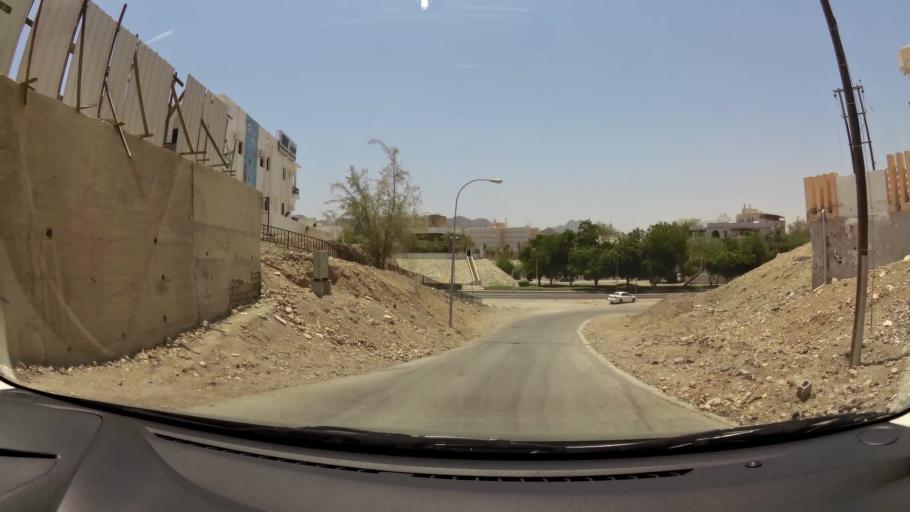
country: OM
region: Muhafazat Masqat
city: Muscat
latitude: 23.6099
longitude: 58.5385
